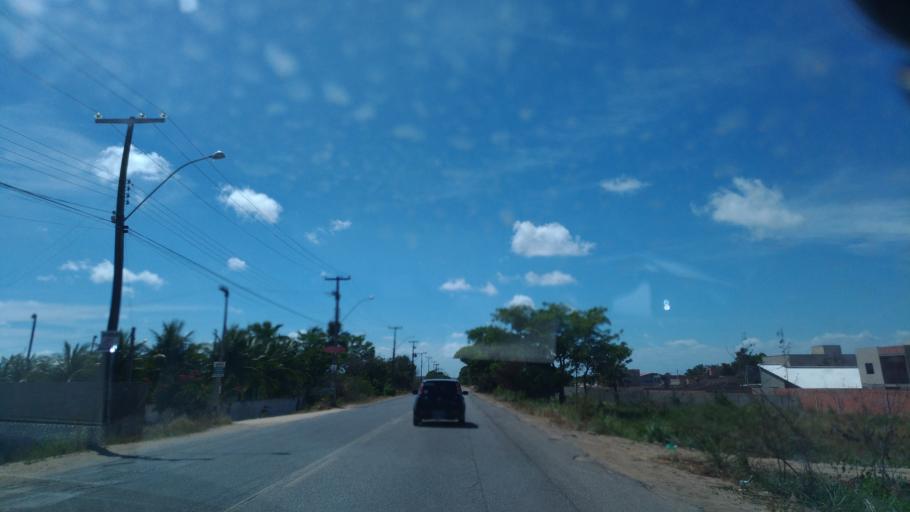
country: BR
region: Alagoas
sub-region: Marechal Deodoro
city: Marechal Deodoro
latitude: -9.7658
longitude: -35.8541
